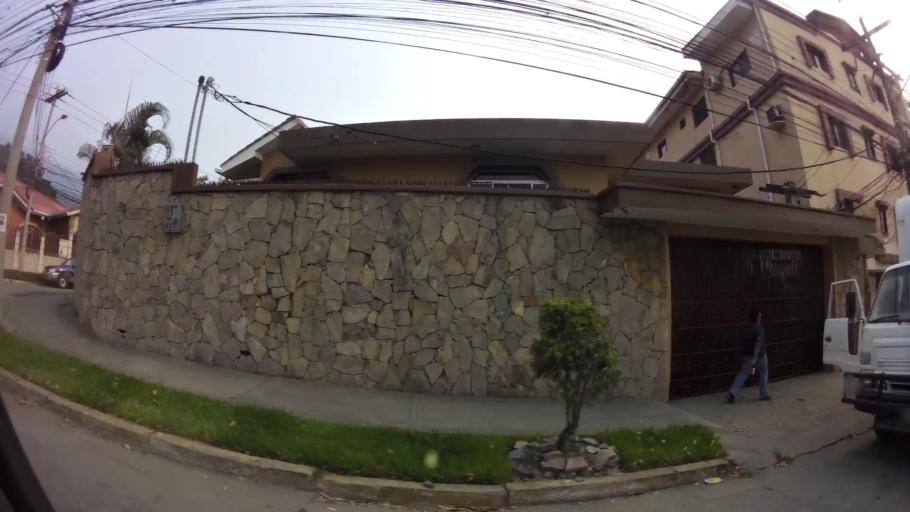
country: HN
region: Cortes
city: Armenta
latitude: 15.4981
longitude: -88.0463
